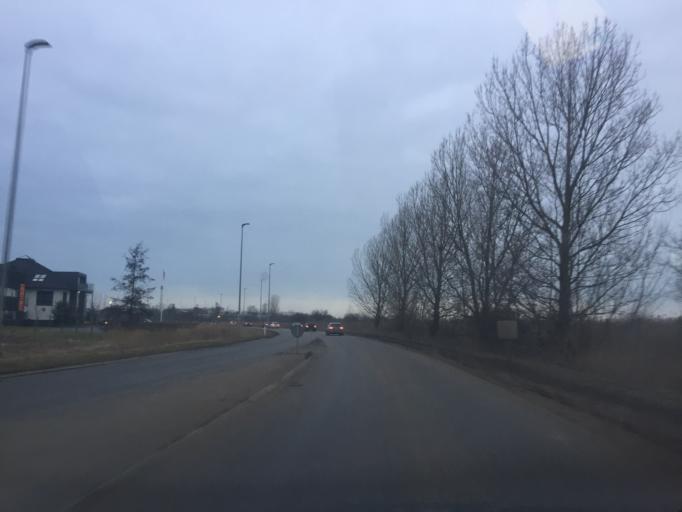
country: DK
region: Zealand
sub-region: Koge Kommune
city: Koge
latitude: 55.4774
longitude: 12.1949
